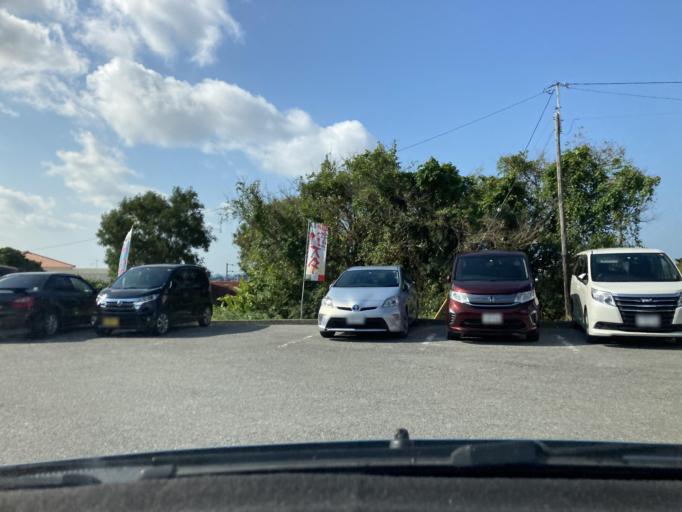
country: JP
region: Okinawa
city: Ginowan
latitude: 26.2481
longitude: 127.7304
